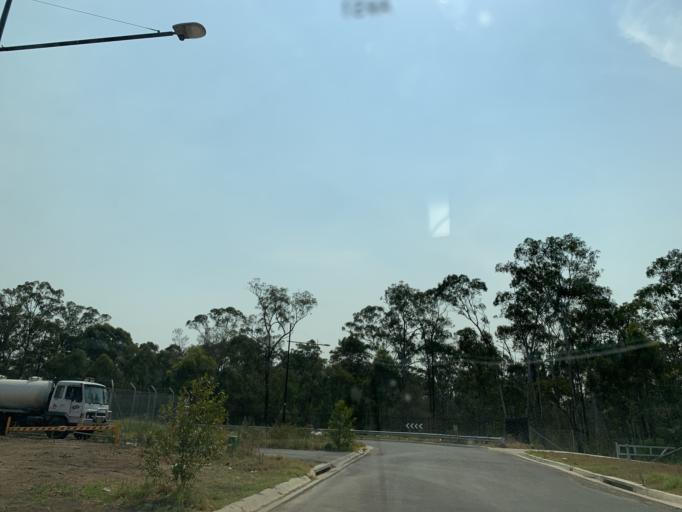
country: AU
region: New South Wales
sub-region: Blacktown
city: Blackett
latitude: -33.7120
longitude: 150.8163
